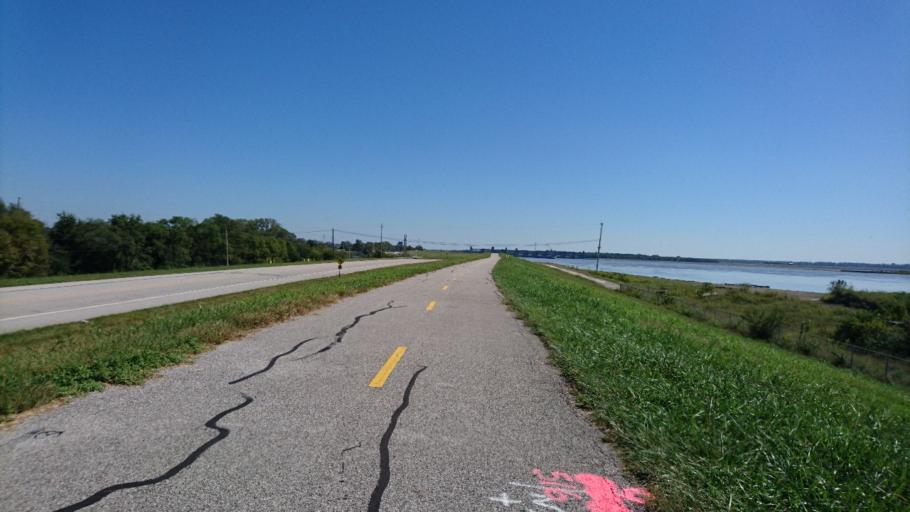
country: US
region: Illinois
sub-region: Madison County
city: Alton
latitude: 38.8841
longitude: -90.1705
